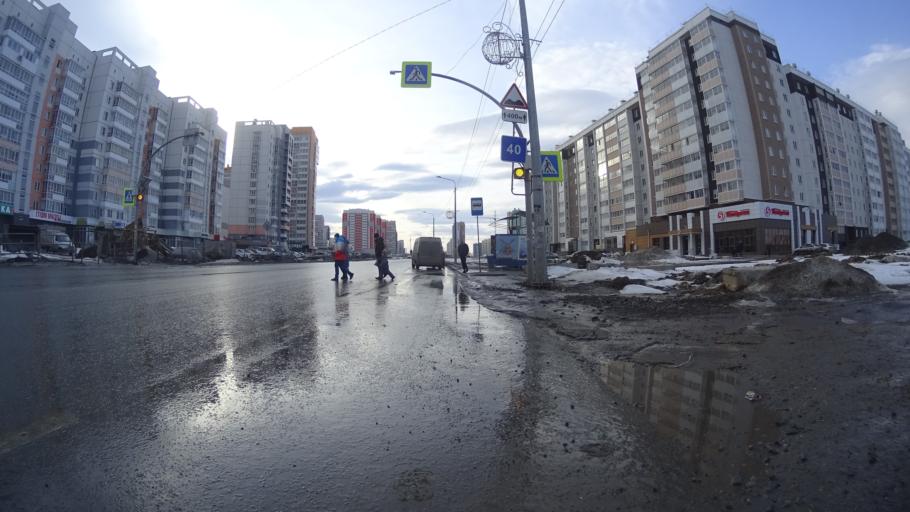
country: RU
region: Chelyabinsk
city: Roshchino
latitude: 55.2096
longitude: 61.2908
